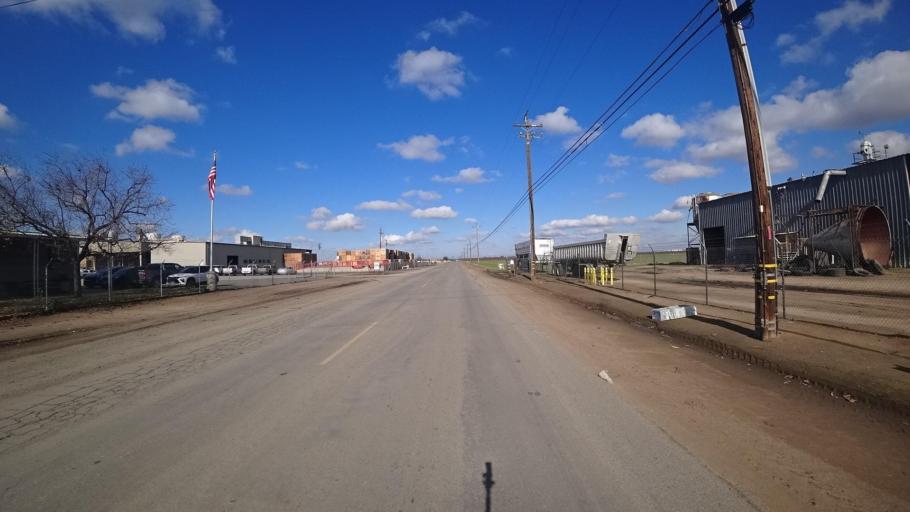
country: US
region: California
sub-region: Kern County
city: McFarland
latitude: 35.6920
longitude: -119.2409
